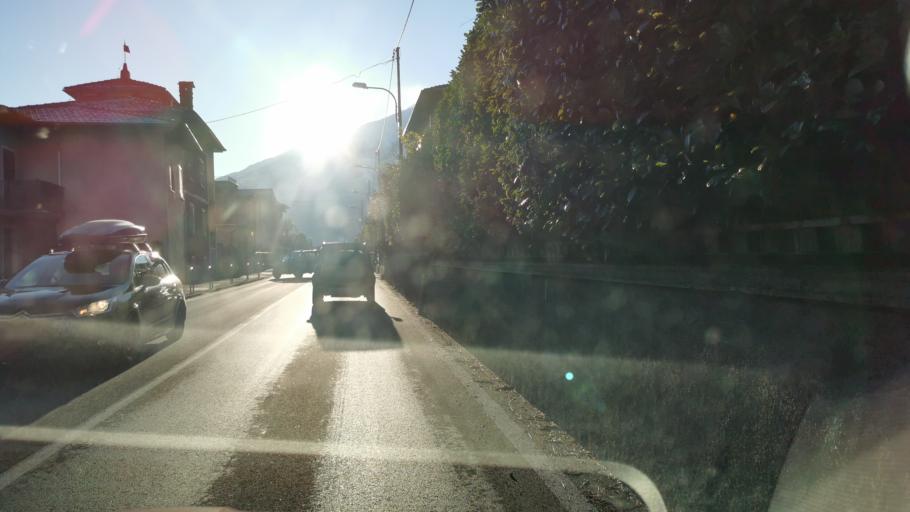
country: IT
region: Lombardy
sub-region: Provincia di Como
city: Gravedona-San Gregorio
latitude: 46.1460
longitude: 9.3020
